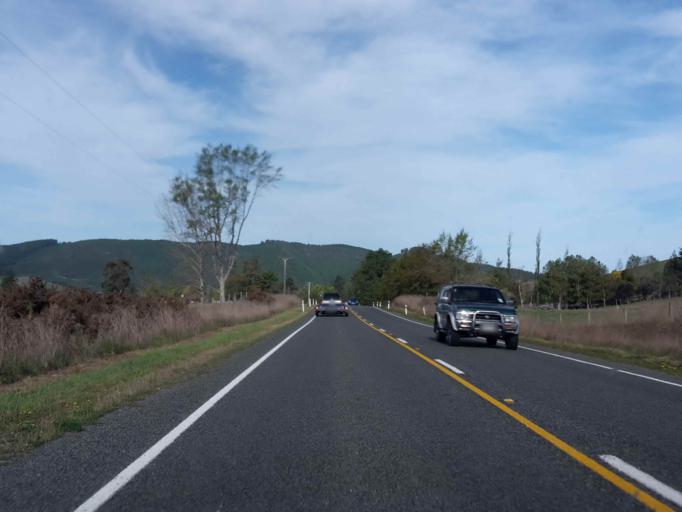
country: NZ
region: Canterbury
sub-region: Timaru District
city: Pleasant Point
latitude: -44.1164
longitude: 171.0212
